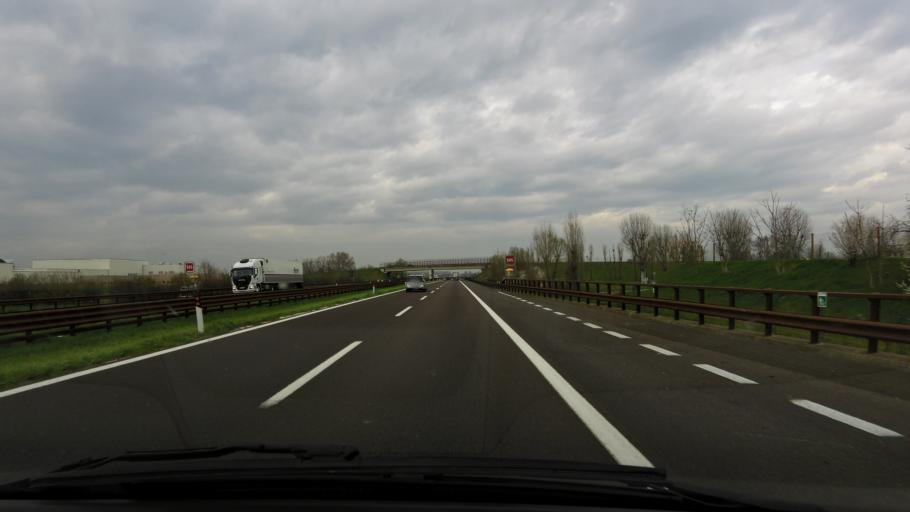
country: IT
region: Emilia-Romagna
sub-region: Provincia di Modena
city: Migliarina
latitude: 44.8002
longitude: 10.8525
